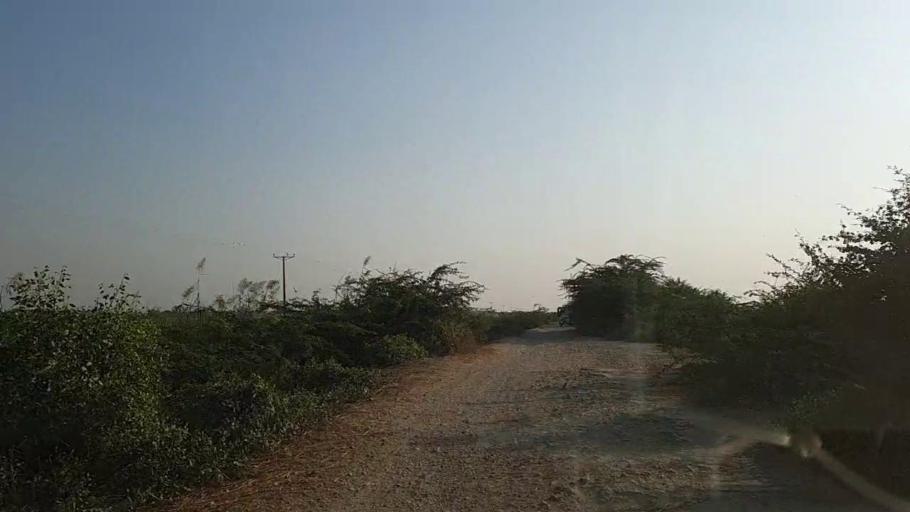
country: PK
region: Sindh
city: Mirpur Batoro
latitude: 24.7636
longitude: 68.2328
